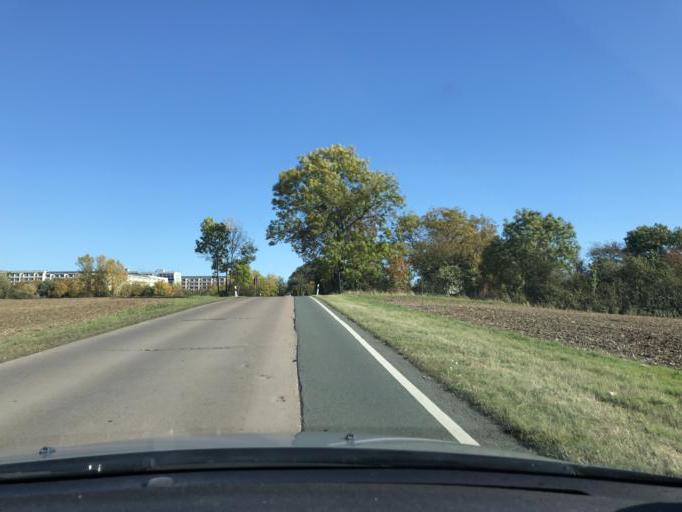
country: DE
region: Thuringia
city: Weimar
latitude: 50.9942
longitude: 11.3001
